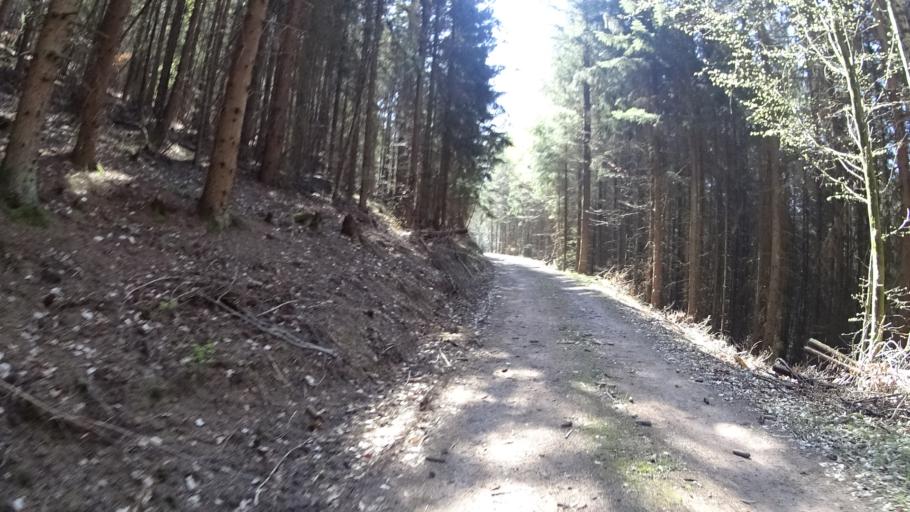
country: DE
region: Rheinland-Pfalz
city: Lambrecht
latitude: 49.3915
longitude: 8.0693
